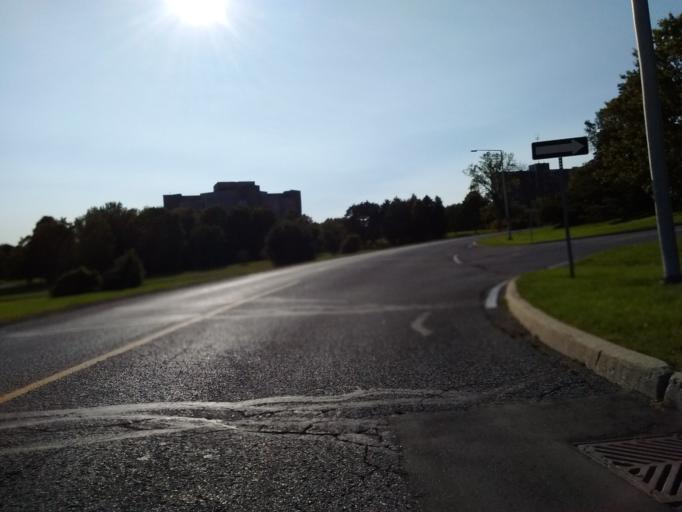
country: CA
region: Ontario
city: Ottawa
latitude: 45.4447
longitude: -75.6155
